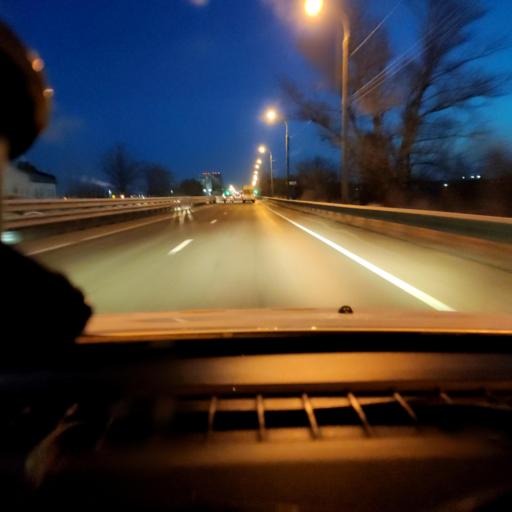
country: RU
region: Samara
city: Samara
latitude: 53.1075
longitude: 50.1639
